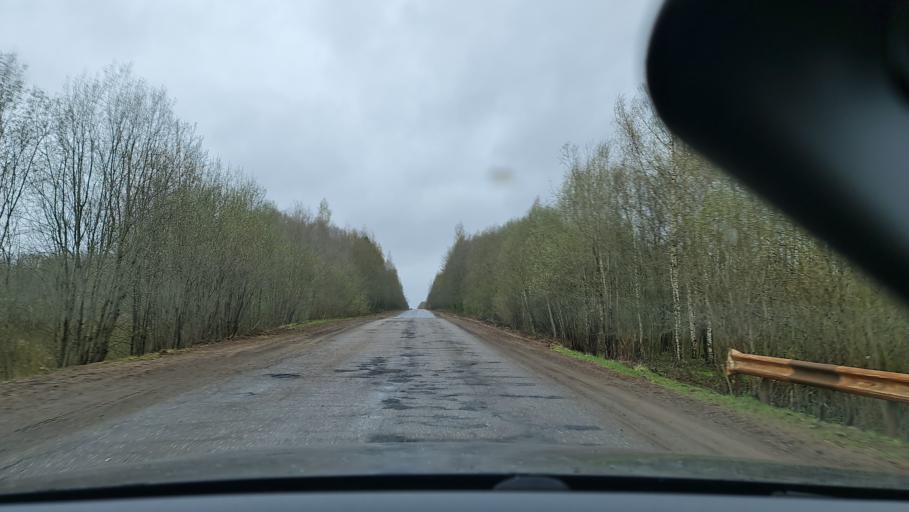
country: RU
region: Novgorod
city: Demyansk
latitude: 57.7414
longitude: 32.5729
